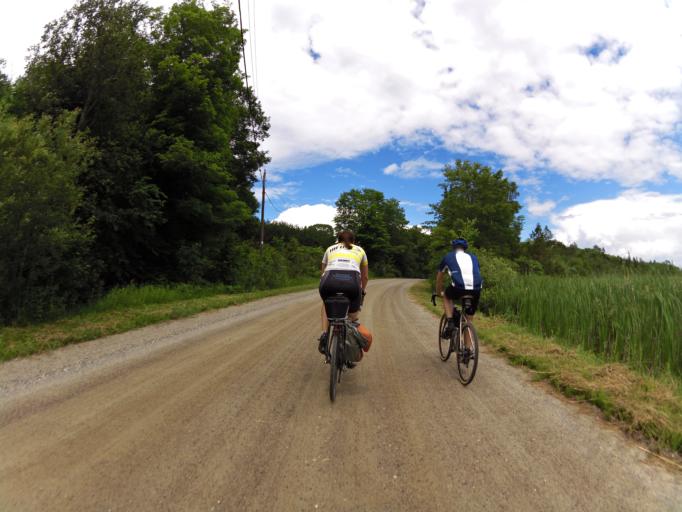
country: CA
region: Ontario
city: Renfrew
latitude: 45.1347
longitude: -76.6721
